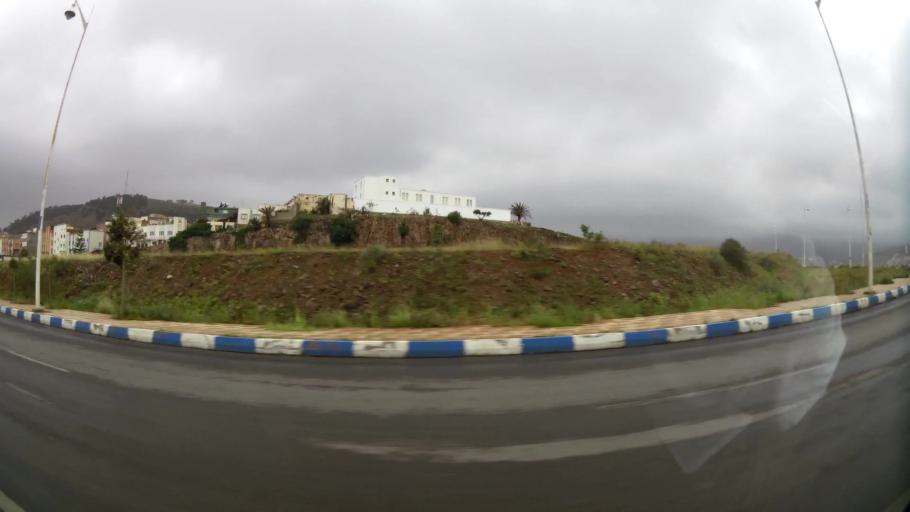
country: MA
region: Oriental
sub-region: Nador
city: Nador
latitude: 35.1892
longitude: -2.9258
